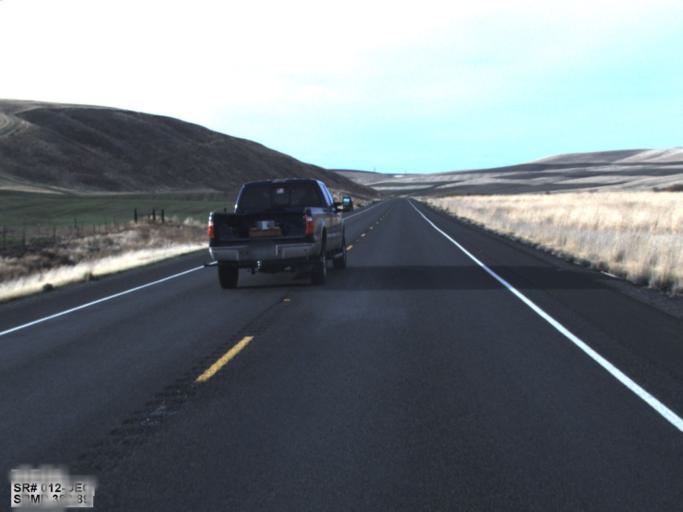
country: US
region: Washington
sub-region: Columbia County
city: Dayton
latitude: 46.5370
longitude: -117.8563
